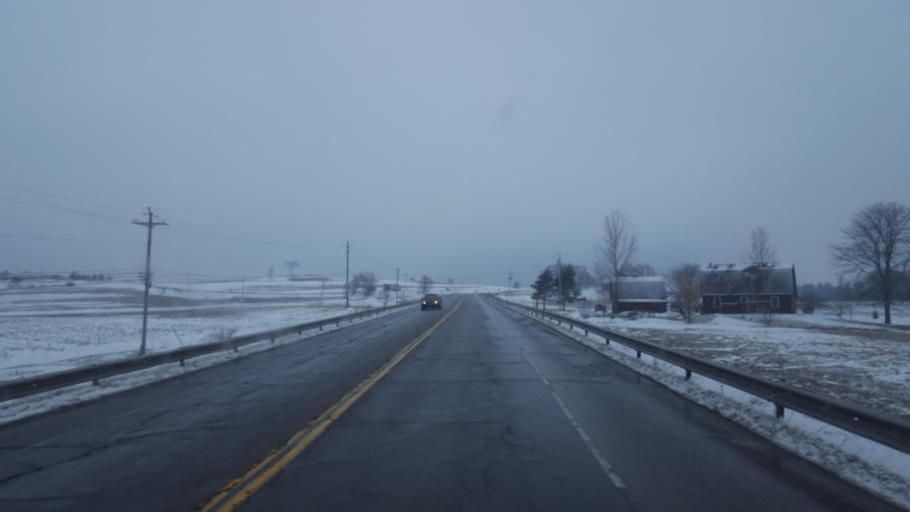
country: US
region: New York
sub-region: Steuben County
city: Canisteo
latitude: 42.1278
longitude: -77.5106
